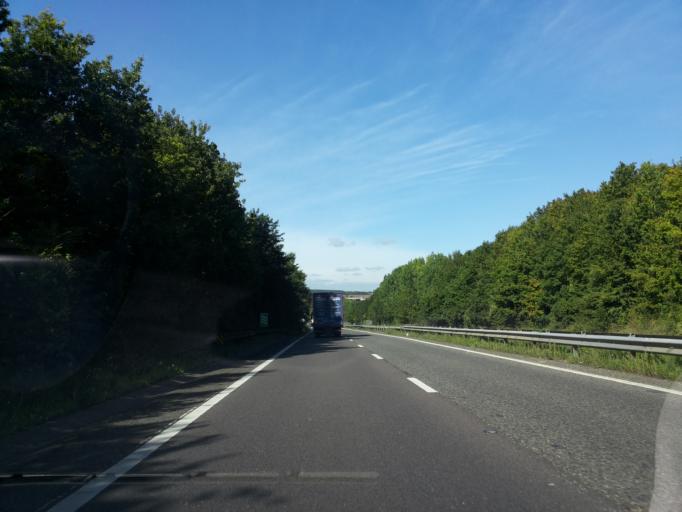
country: GB
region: England
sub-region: Kent
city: Canterbury
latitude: 51.2643
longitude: 1.0698
